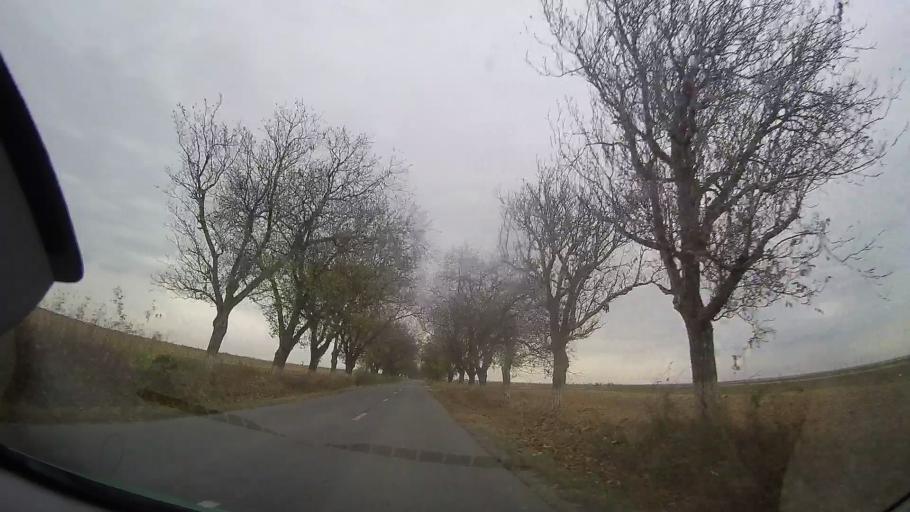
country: RO
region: Prahova
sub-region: Comuna Fantanele
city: Fantanele
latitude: 45.0162
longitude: 26.4028
